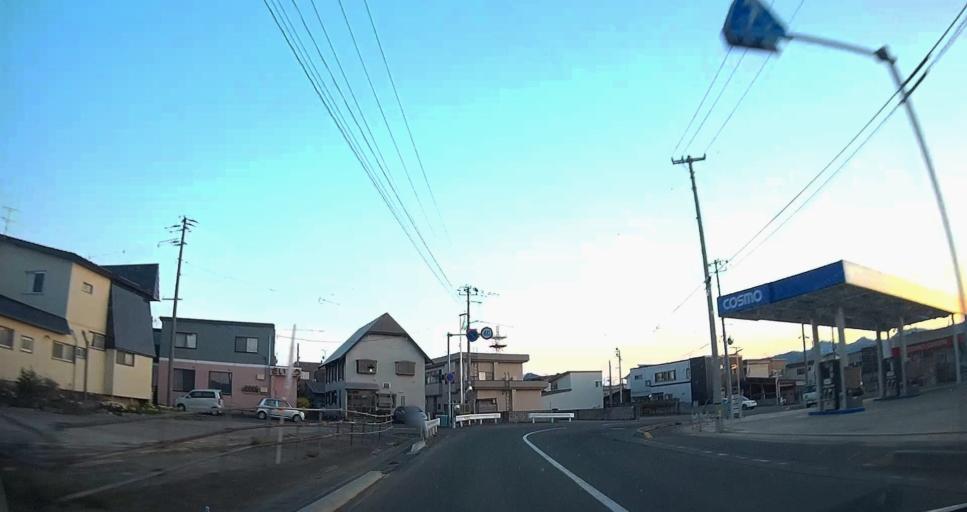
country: JP
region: Aomori
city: Misawa
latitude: 40.8683
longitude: 141.1297
